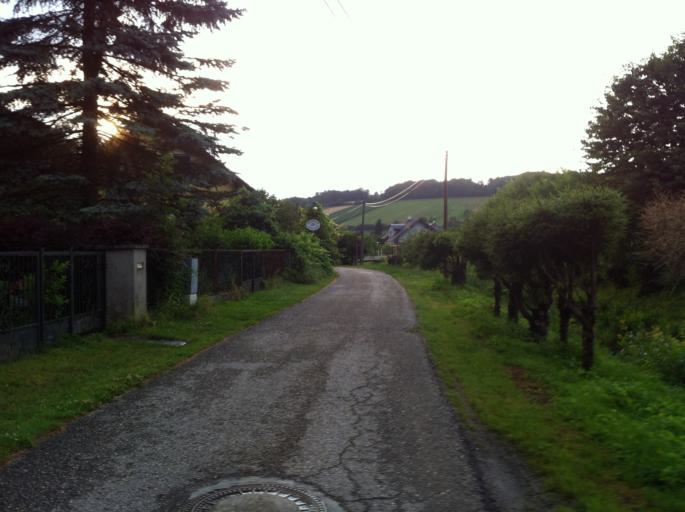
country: AT
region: Lower Austria
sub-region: Politischer Bezirk Tulln
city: Sieghartskirchen
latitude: 48.2493
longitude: 16.0453
